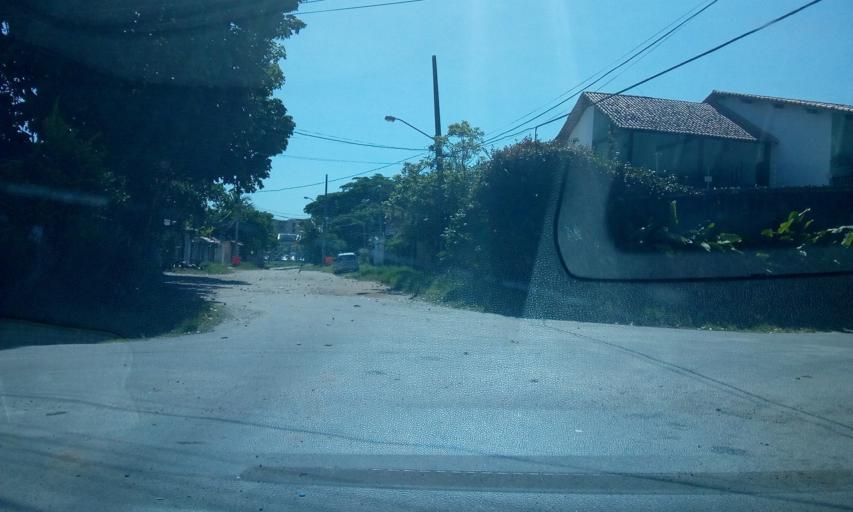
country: BR
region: Rio de Janeiro
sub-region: Nilopolis
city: Nilopolis
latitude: -23.0286
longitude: -43.4788
